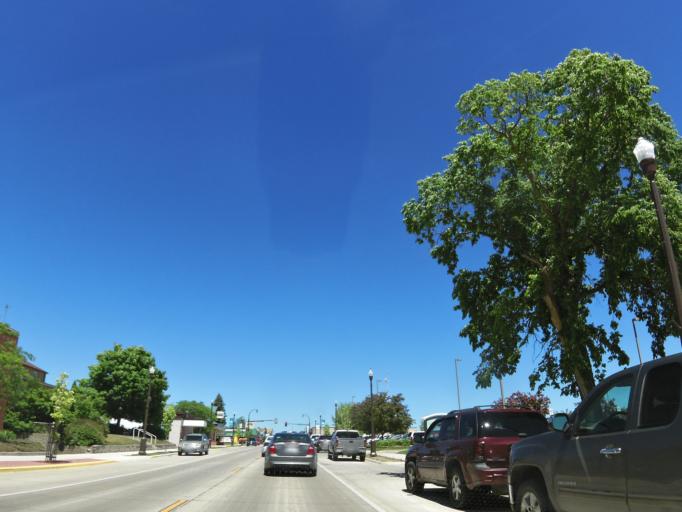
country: US
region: Minnesota
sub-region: Becker County
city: Detroit Lakes
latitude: 46.8145
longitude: -95.8455
